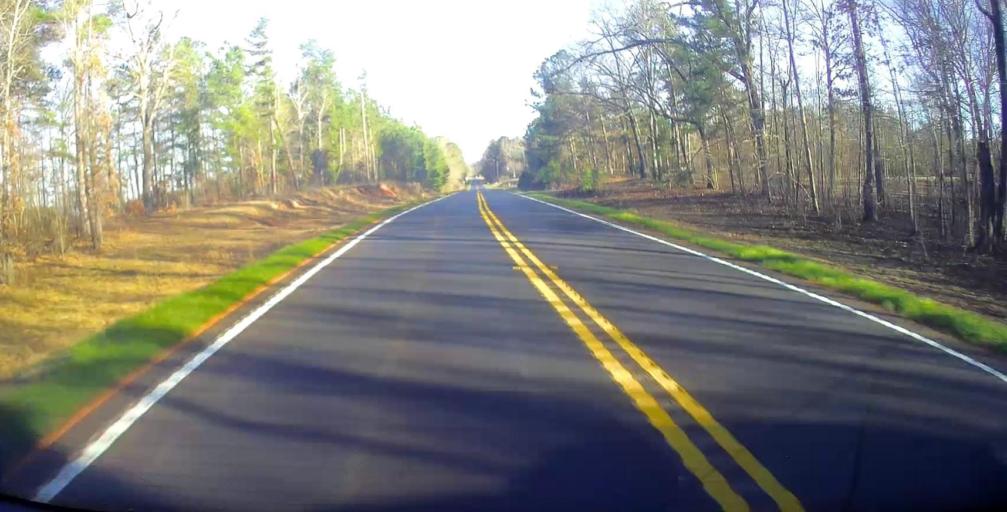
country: US
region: Georgia
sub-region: Meriwether County
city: Greenville
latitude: 32.9119
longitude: -84.7301
